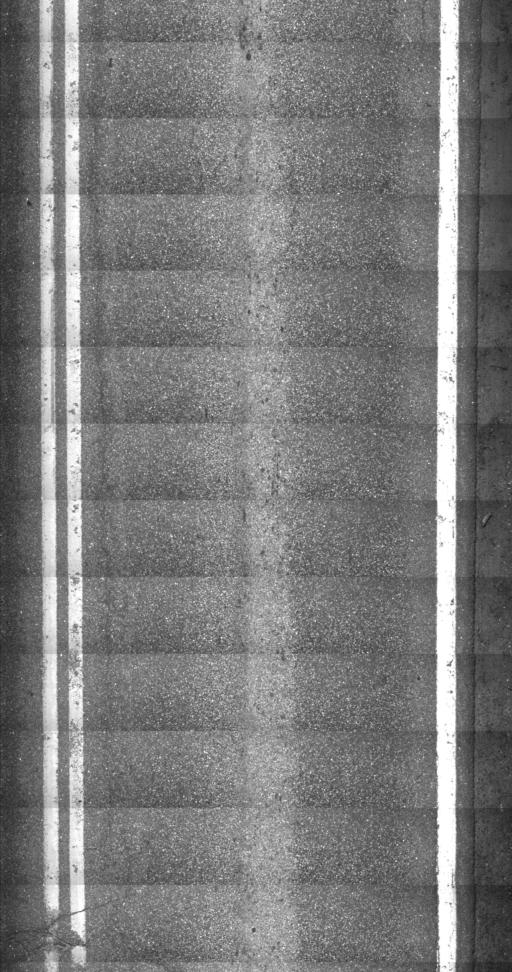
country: US
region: New Hampshire
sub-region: Sullivan County
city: Charlestown
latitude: 43.2619
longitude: -72.4281
